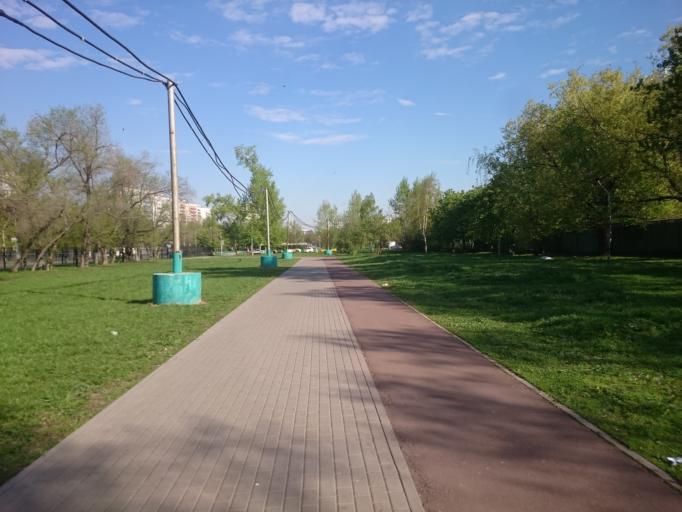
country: RU
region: Moscow
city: Tekstil'shchiki
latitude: 55.7154
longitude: 37.7438
